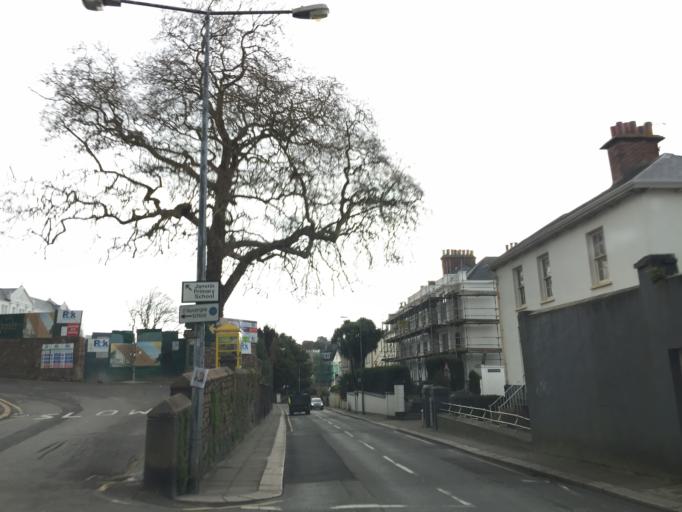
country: JE
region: St Helier
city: Saint Helier
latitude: 49.1931
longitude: -2.1044
